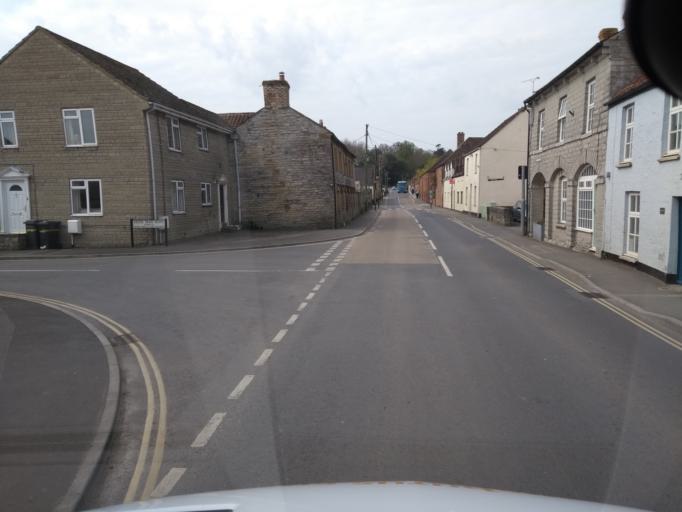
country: GB
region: England
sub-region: Somerset
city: Langport
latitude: 51.0366
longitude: -2.8330
